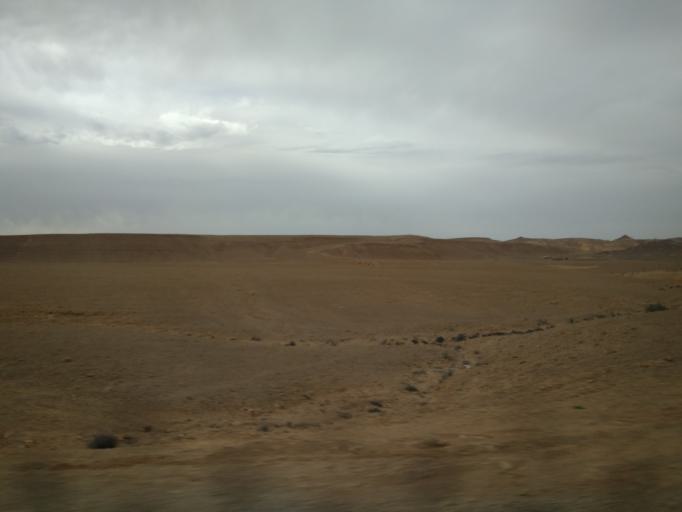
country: IL
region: Southern District
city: Eilat
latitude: 29.8560
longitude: 34.8439
